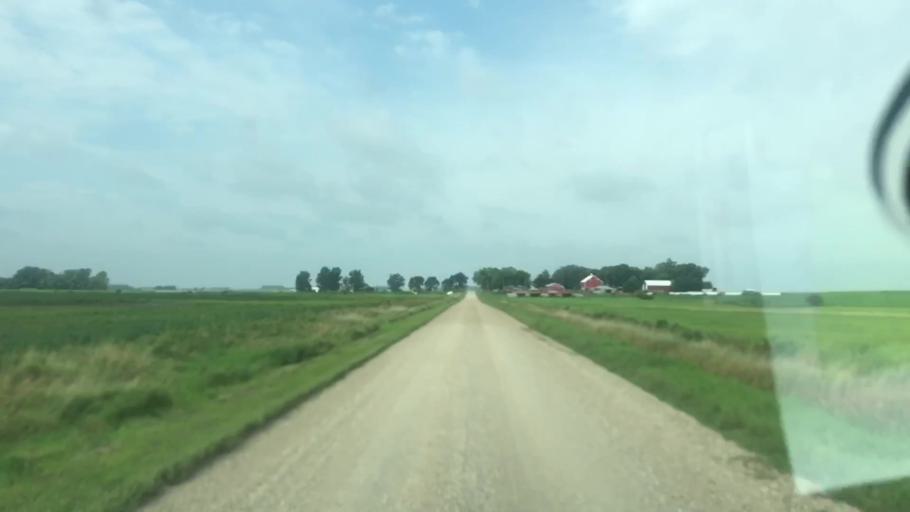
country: US
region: Iowa
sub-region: O'Brien County
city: Sheldon
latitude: 43.2725
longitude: -95.9126
